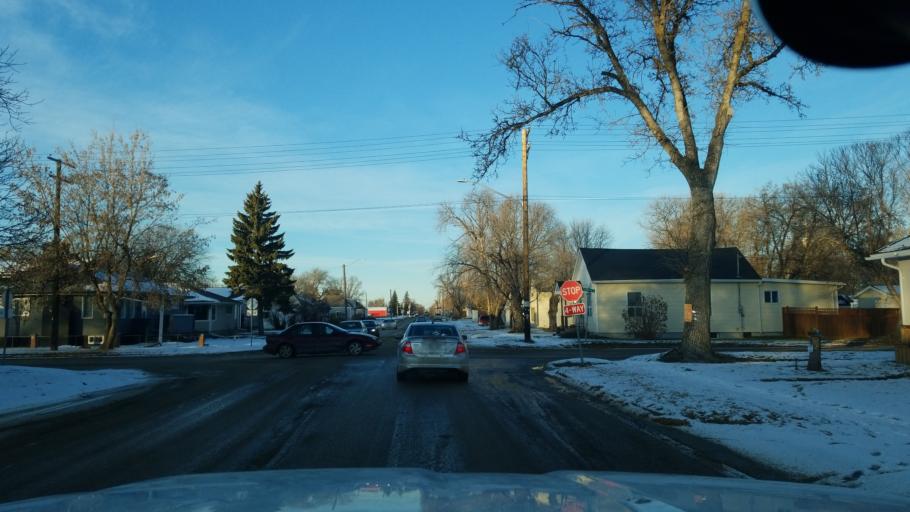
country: CA
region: Manitoba
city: Portage la Prairie
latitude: 49.9754
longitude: -98.3013
